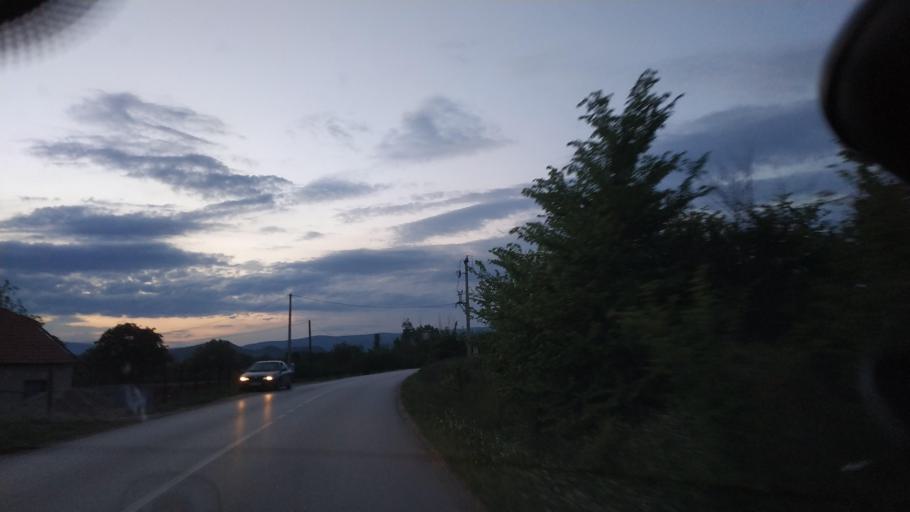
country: RS
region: Central Serbia
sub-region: Nisavski Okrug
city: Merosina
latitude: 43.2923
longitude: 21.7076
